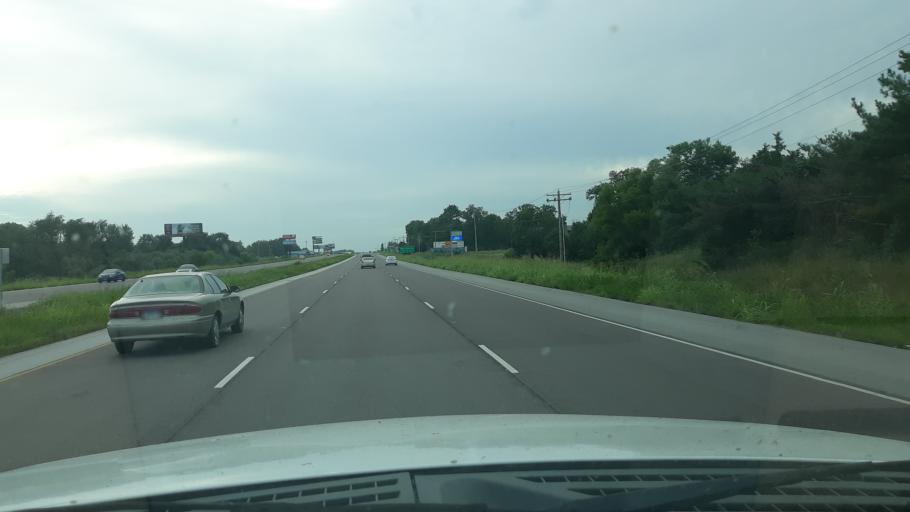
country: US
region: Illinois
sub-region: Williamson County
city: Energy
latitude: 37.7451
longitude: -89.0373
